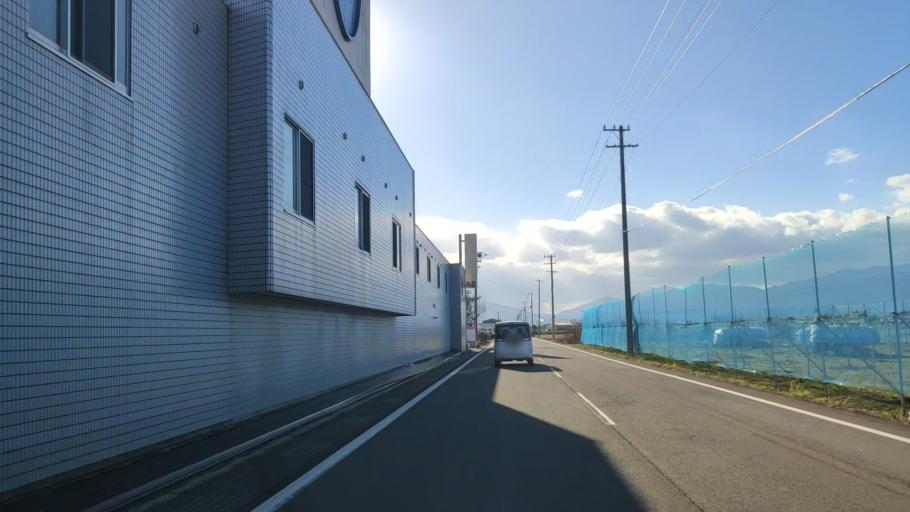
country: JP
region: Ehime
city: Saijo
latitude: 33.9147
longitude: 133.1178
